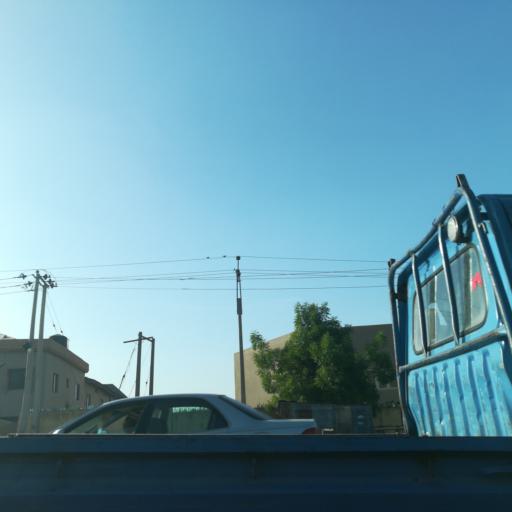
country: NG
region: Kano
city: Kano
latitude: 12.0123
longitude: 8.4993
